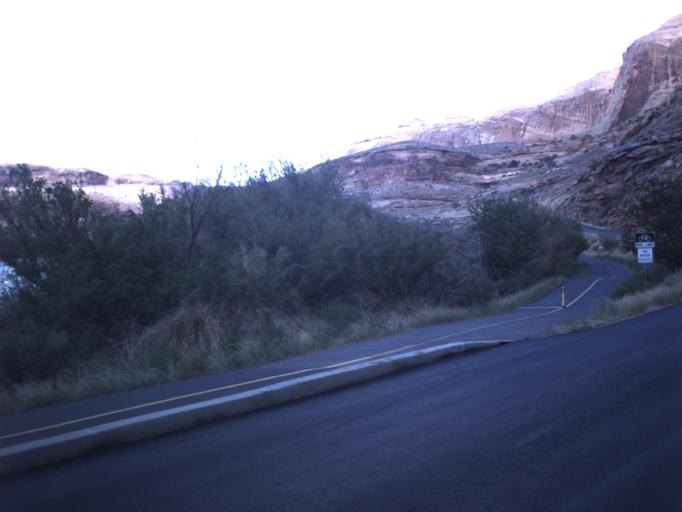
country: US
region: Utah
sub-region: Grand County
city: Moab
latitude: 38.6015
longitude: -109.5629
